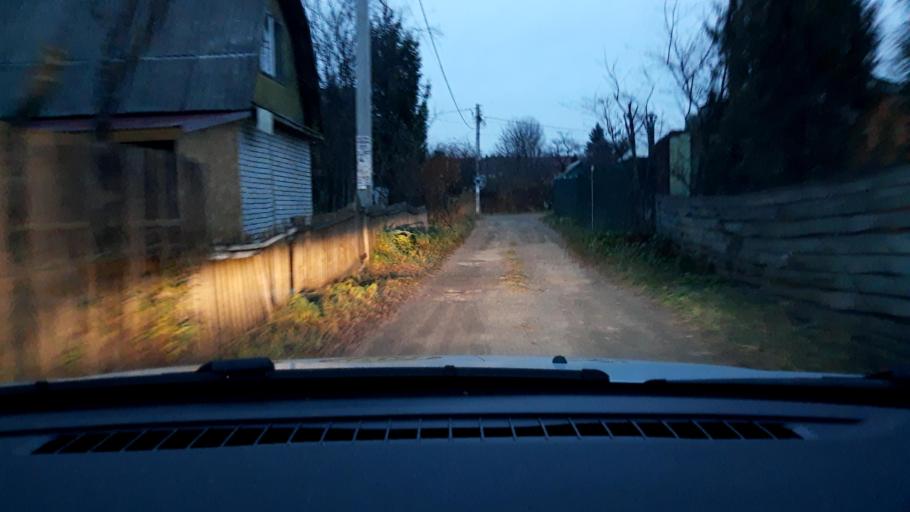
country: RU
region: Nizjnij Novgorod
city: Neklyudovo
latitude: 56.4301
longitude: 44.0091
